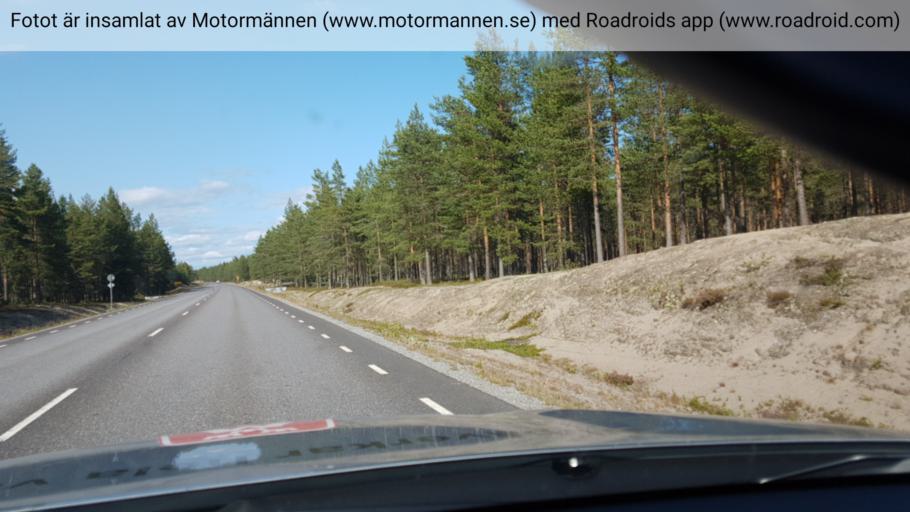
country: SE
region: Norrbotten
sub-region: Pitea Kommun
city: Pitea
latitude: 65.2471
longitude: 21.5341
